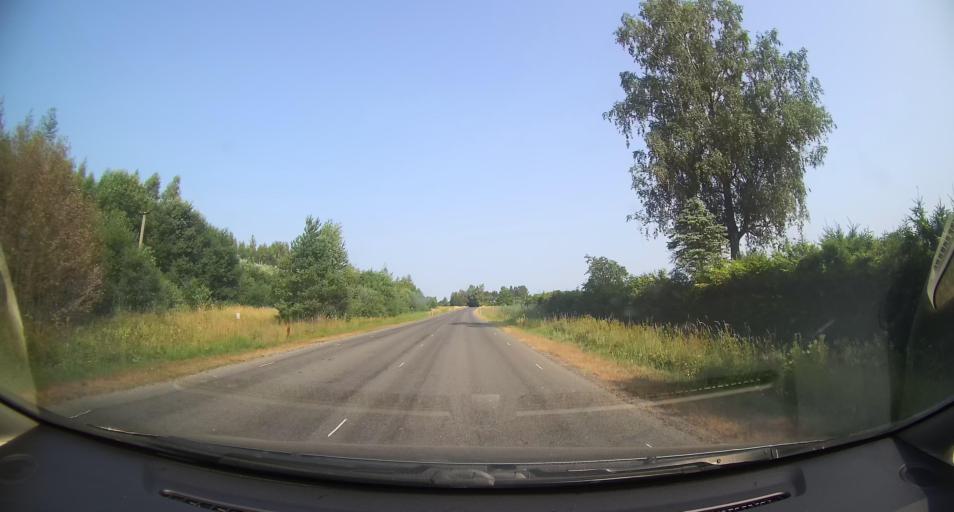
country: EE
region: Paernumaa
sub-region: Audru vald
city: Audru
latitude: 58.4314
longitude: 24.3143
